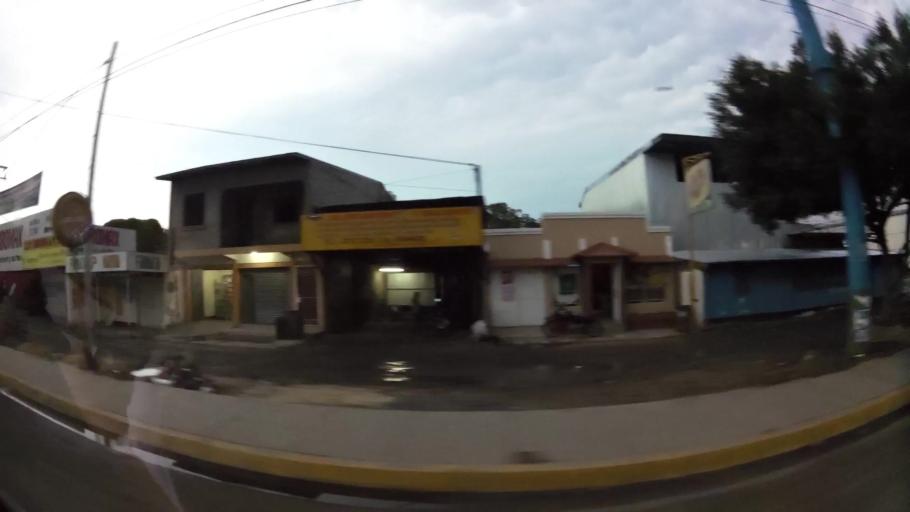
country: NI
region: Esteli
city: Esteli
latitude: 13.0904
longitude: -86.3516
